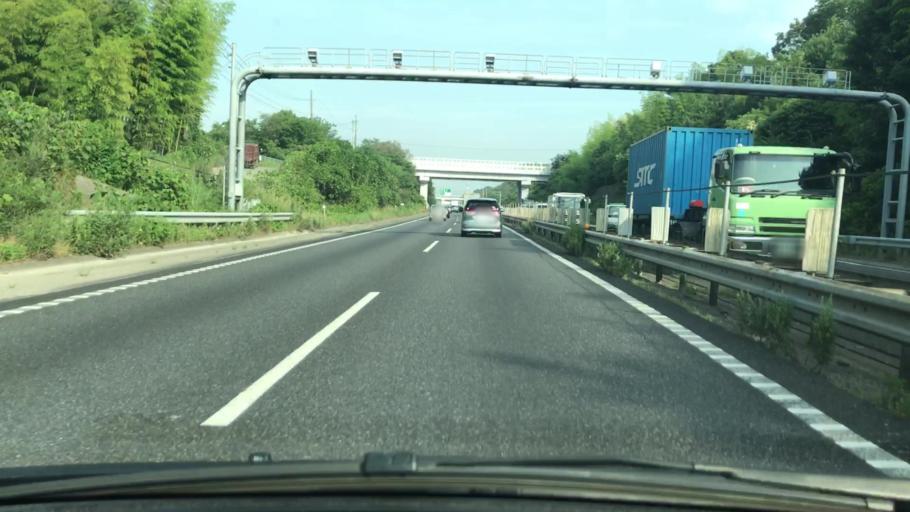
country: JP
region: Hyogo
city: Akashi
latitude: 34.7007
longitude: 134.9629
